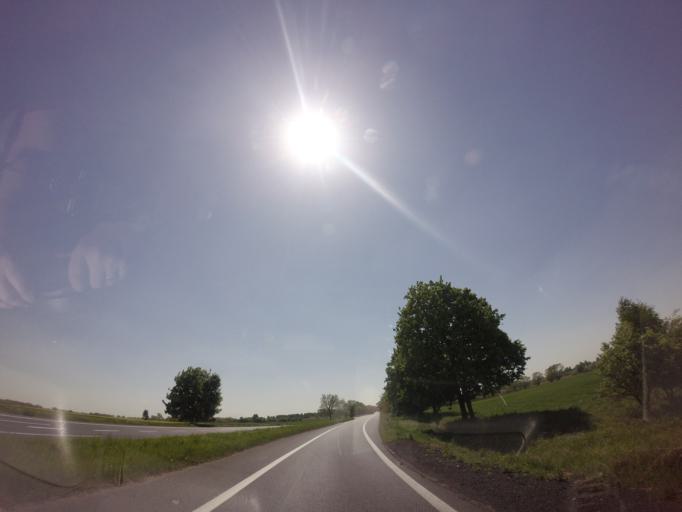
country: PL
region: West Pomeranian Voivodeship
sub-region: Powiat pyrzycki
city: Lipiany
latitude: 52.9881
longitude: 14.9794
